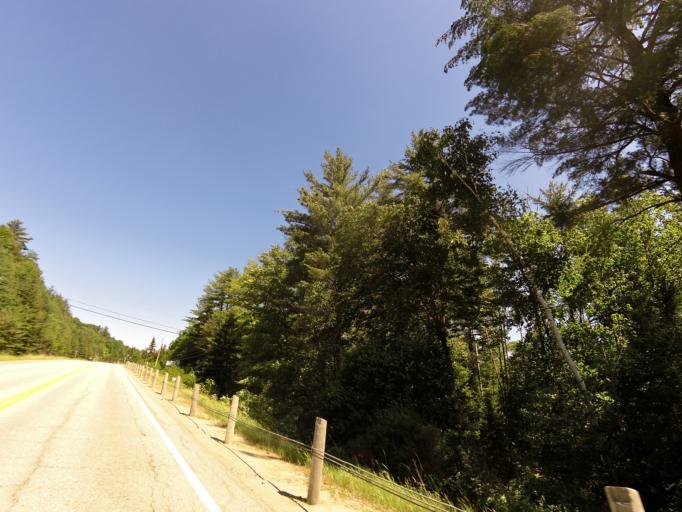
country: CA
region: Quebec
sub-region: Abitibi-Temiscamingue
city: Temiscaming
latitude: 46.7024
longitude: -79.1021
